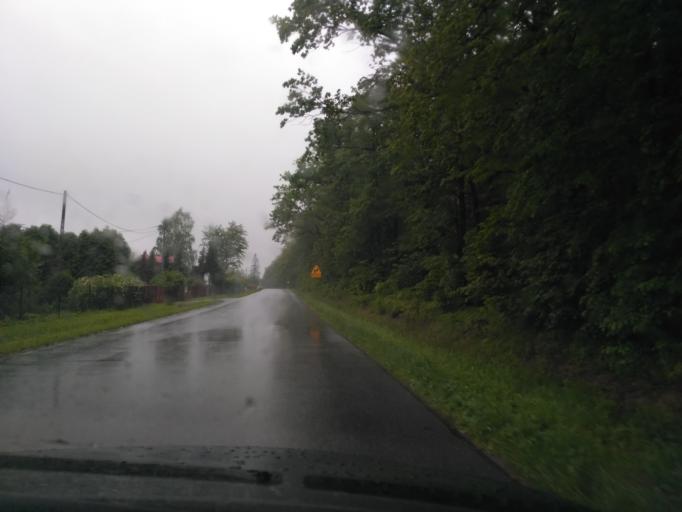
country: PL
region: Subcarpathian Voivodeship
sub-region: Powiat jasielski
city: Debowiec
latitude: 49.6577
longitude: 21.4208
